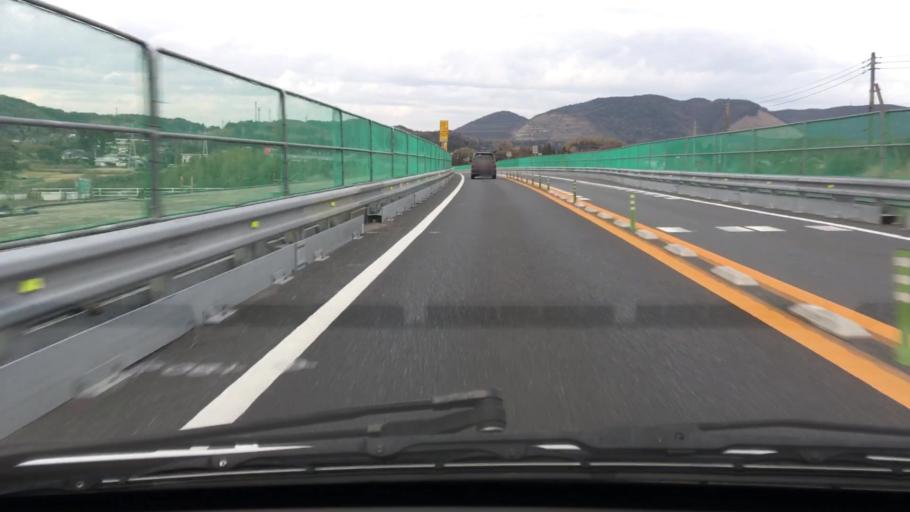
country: JP
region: Chiba
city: Kimitsu
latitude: 35.2112
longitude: 139.8839
